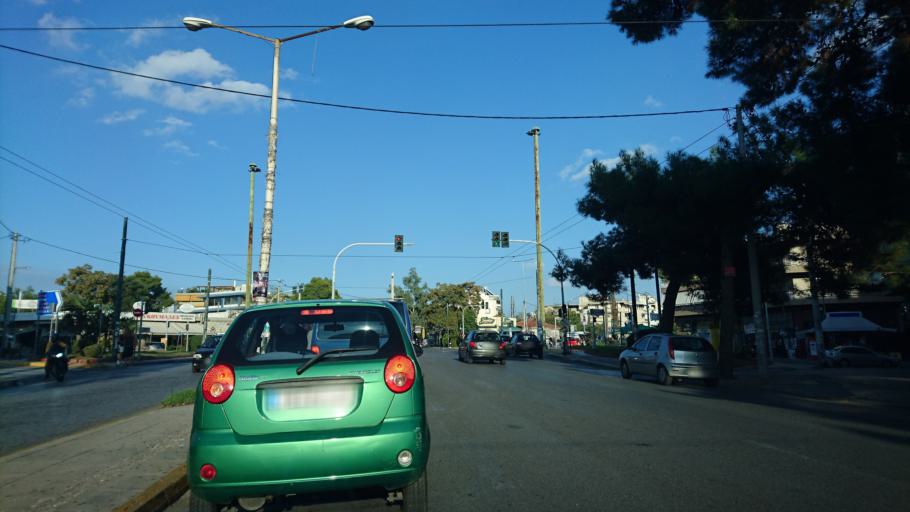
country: GR
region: Attica
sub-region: Nomarchia Athinas
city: Khalandrion
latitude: 38.0188
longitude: 23.8067
